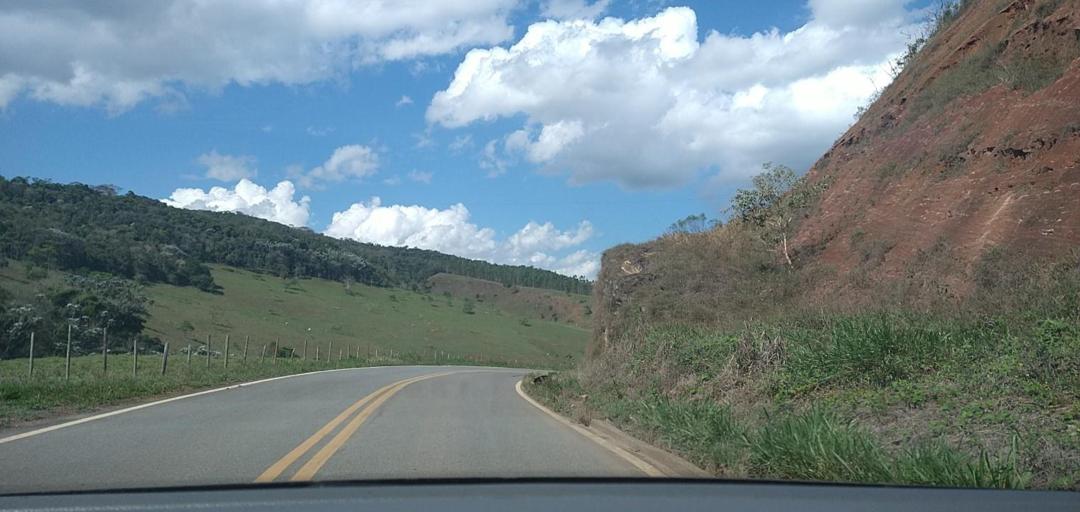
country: BR
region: Minas Gerais
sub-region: Rio Piracicaba
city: Rio Piracicaba
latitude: -19.9805
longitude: -43.1310
